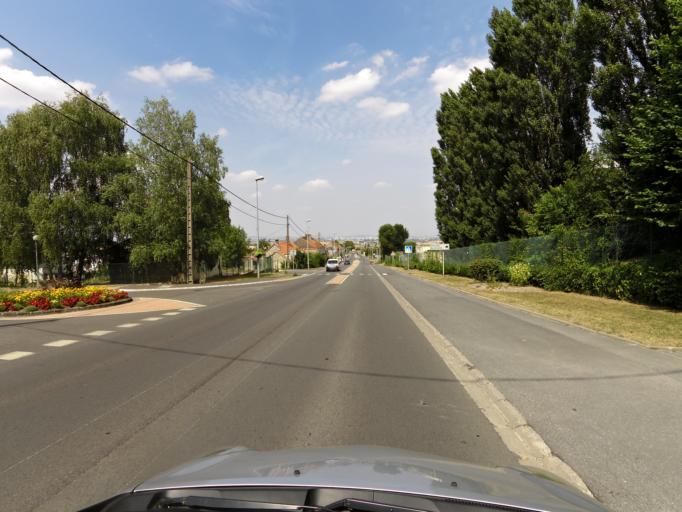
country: FR
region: Champagne-Ardenne
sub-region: Departement de la Marne
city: Rilly-la-Montagne
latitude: 49.1626
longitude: 4.0115
